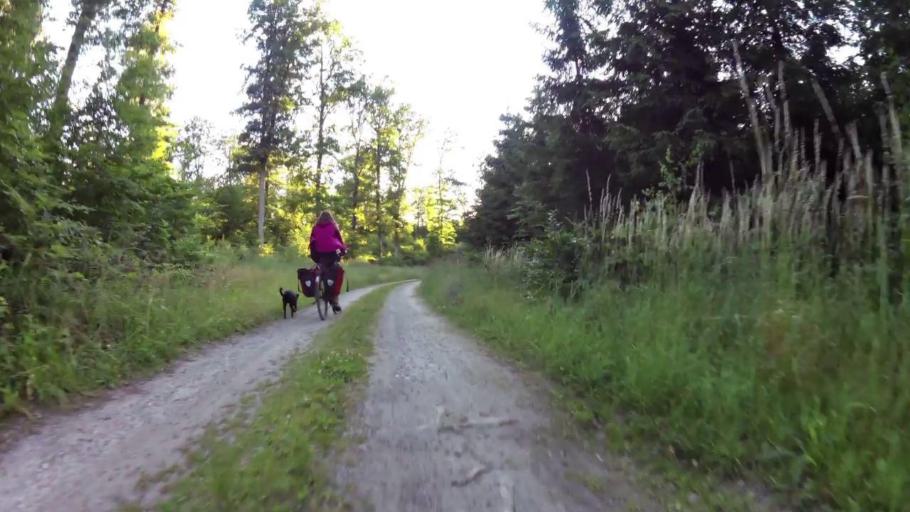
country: PL
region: West Pomeranian Voivodeship
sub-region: Powiat lobeski
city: Lobez
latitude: 53.7511
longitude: 15.6347
